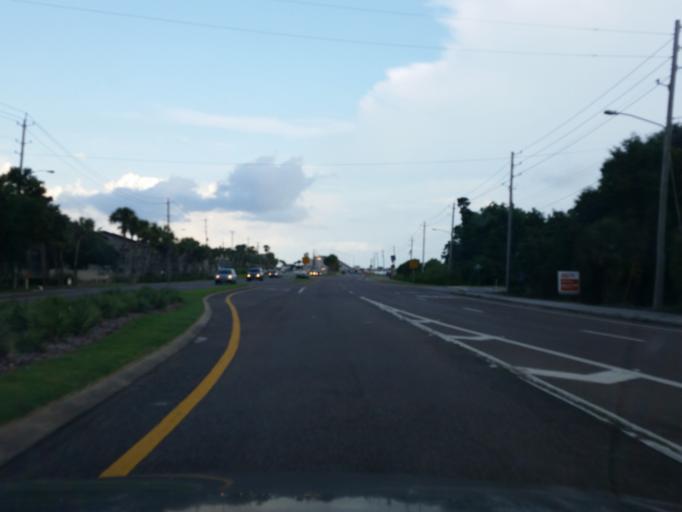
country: US
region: Florida
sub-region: Santa Rosa County
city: Gulf Breeze
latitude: 30.3561
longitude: -87.1590
